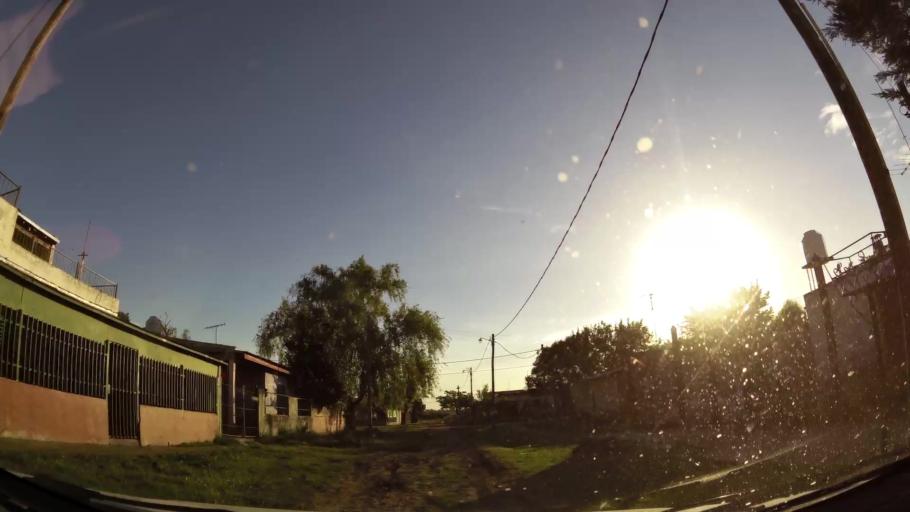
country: AR
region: Buenos Aires
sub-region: Partido de Merlo
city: Merlo
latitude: -34.7000
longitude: -58.7552
